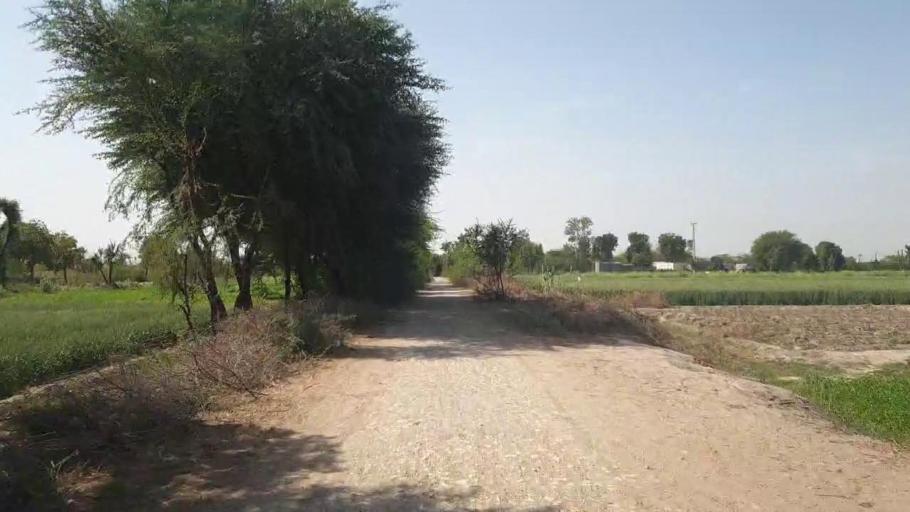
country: PK
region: Sindh
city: Kunri
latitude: 25.2673
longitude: 69.6370
